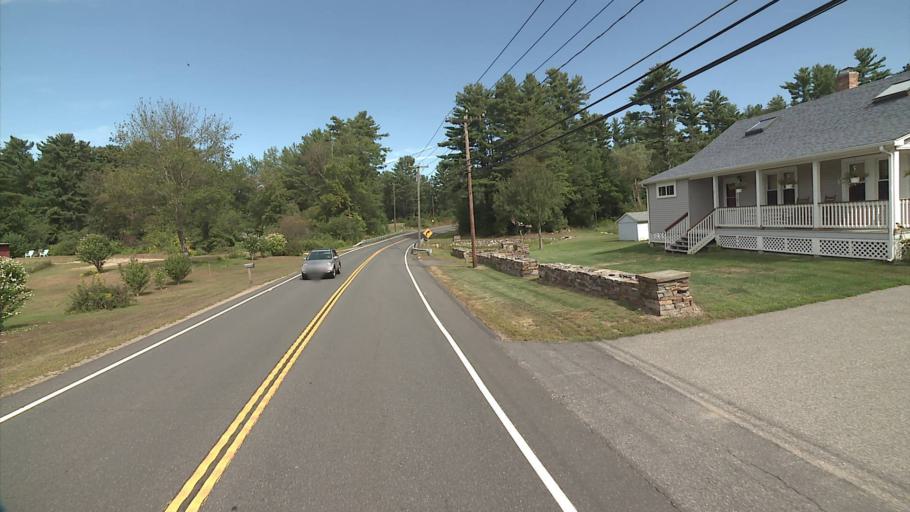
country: US
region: Connecticut
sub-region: Tolland County
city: Stafford
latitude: 41.9872
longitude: -72.3176
